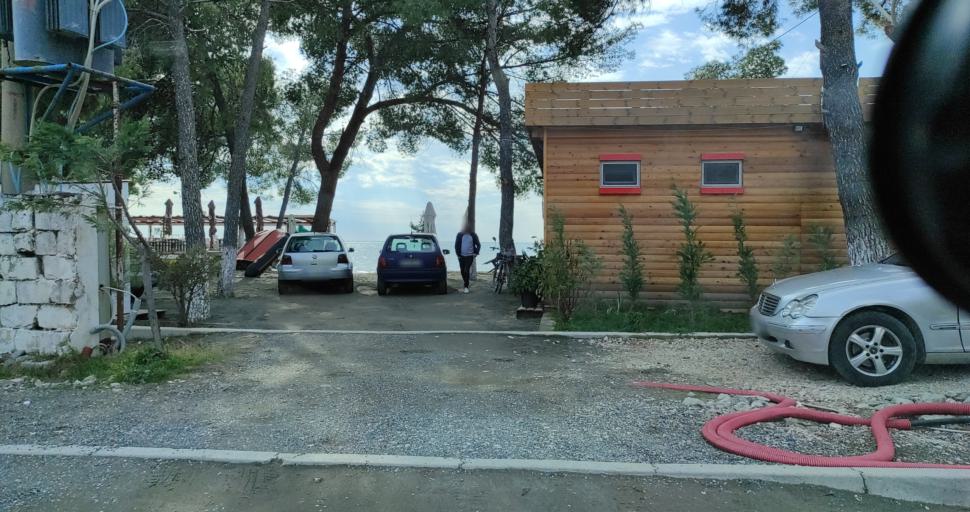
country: AL
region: Lezhe
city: Shengjin
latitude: 41.7944
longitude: 19.6023
